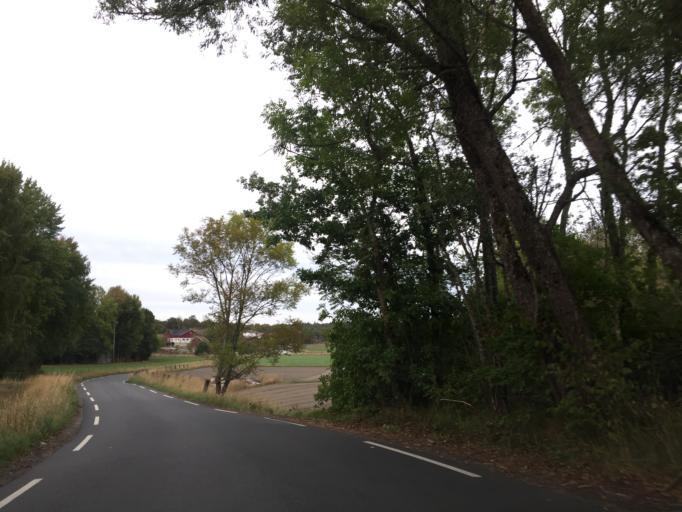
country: NO
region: Ostfold
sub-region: Hvaler
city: Skjaerhalden
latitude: 59.0423
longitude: 11.0312
